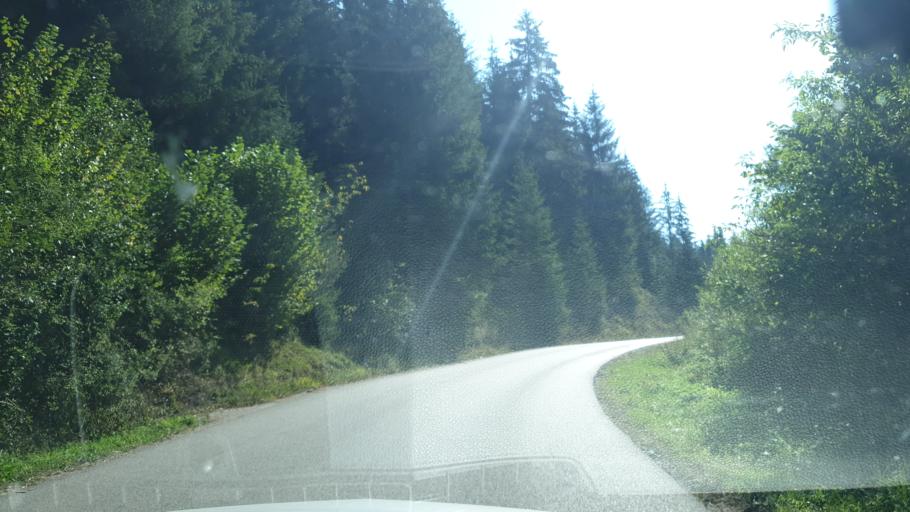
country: RS
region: Central Serbia
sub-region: Zlatiborski Okrug
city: Nova Varos
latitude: 43.4508
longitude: 19.8442
